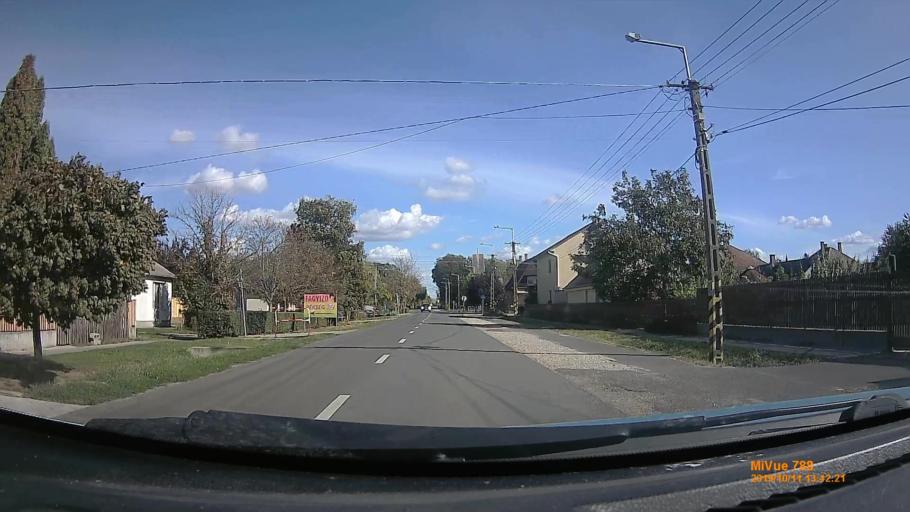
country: HU
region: Hajdu-Bihar
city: Balmazujvaros
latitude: 47.5393
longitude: 21.3425
